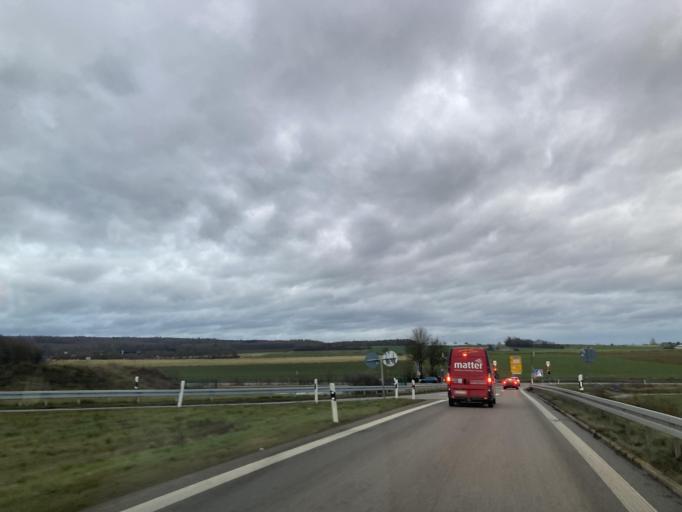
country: DE
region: Baden-Wuerttemberg
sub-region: Tuebingen Region
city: Langenau
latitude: 48.4920
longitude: 10.0906
